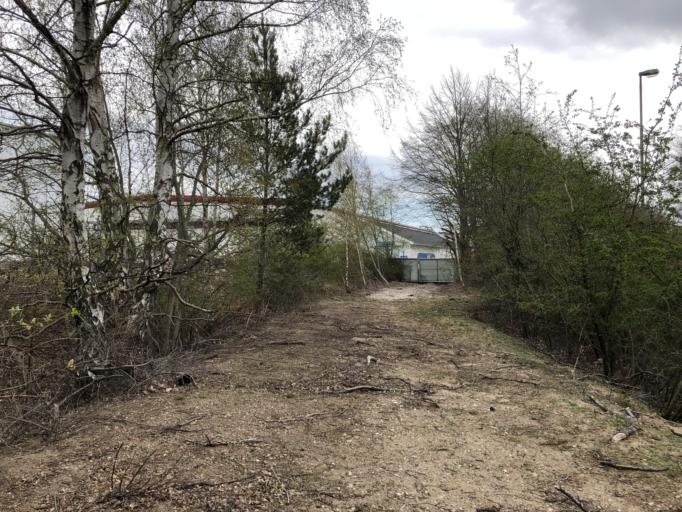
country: SE
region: Skane
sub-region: Malmo
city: Tygelsjo
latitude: 55.5536
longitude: 13.0407
